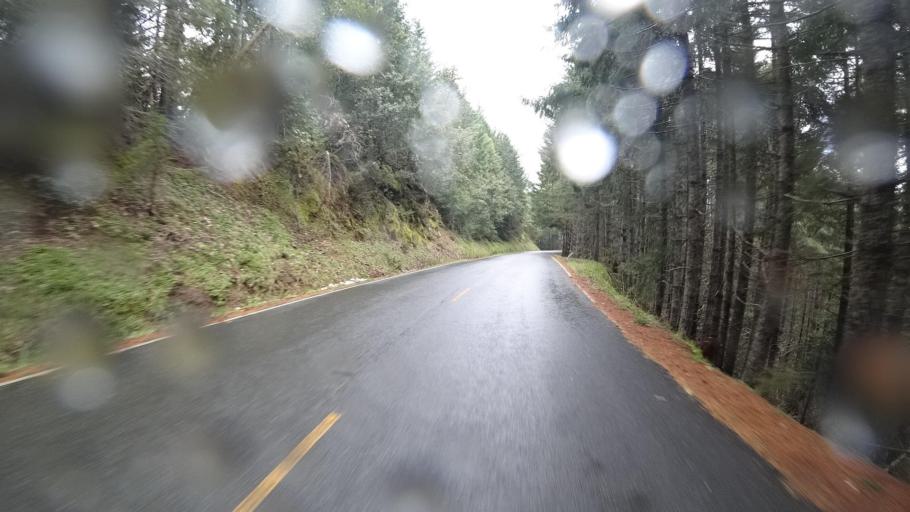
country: US
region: California
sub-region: Humboldt County
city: Westhaven-Moonstone
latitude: 41.1480
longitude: -123.8405
